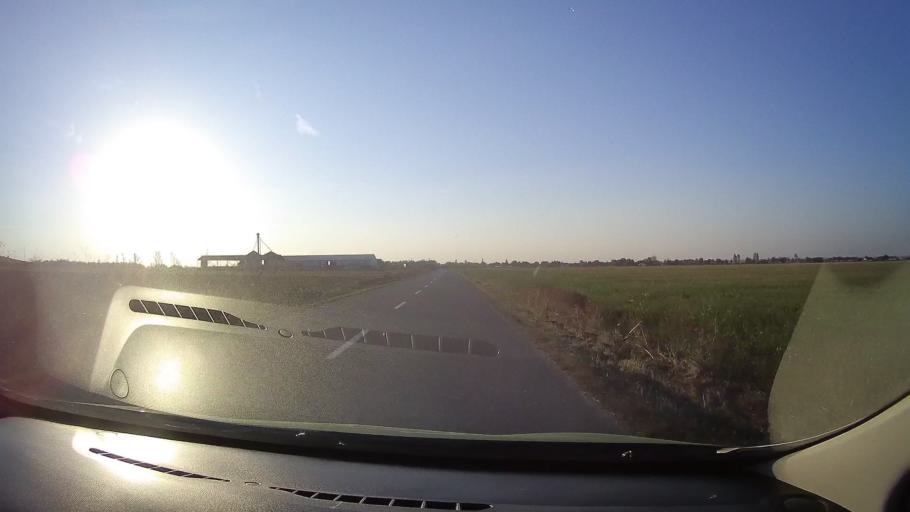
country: RO
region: Bihor
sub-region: Comuna Biharea
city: Biharea
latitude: 47.1628
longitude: 21.9589
